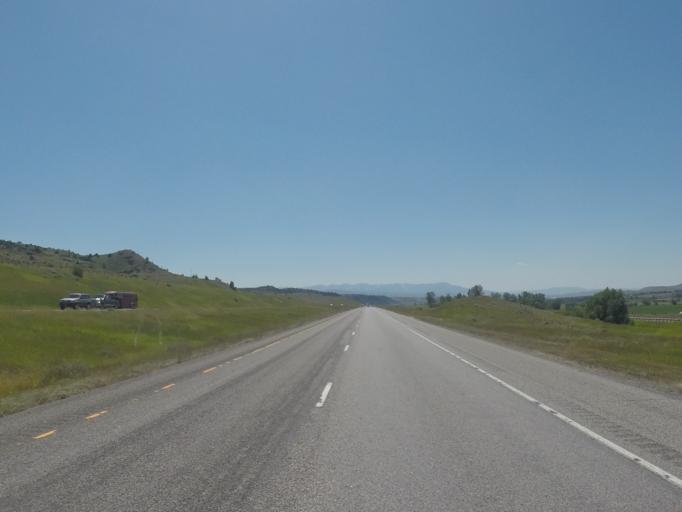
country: US
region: Montana
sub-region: Sweet Grass County
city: Big Timber
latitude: 45.7984
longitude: -110.0317
